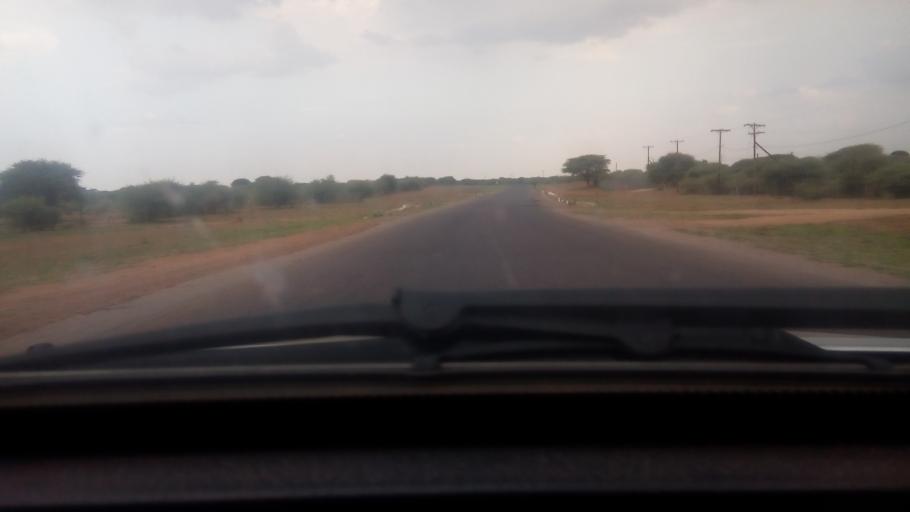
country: BW
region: Kweneng
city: Metsemotlhaba
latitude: -24.4656
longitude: 25.6722
